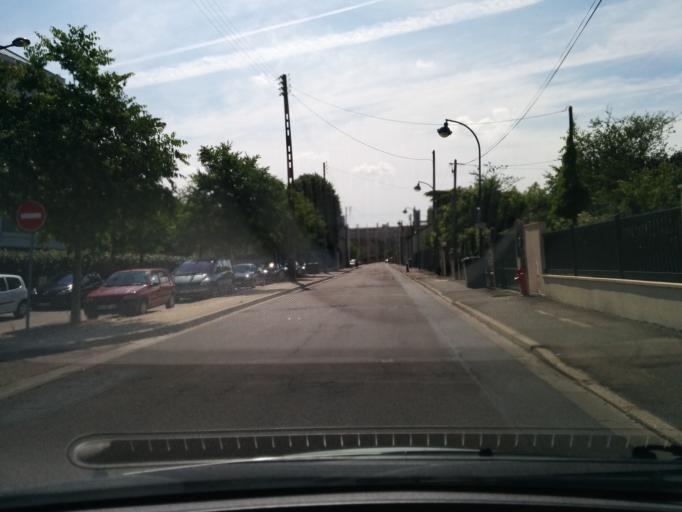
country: FR
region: Ile-de-France
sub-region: Departement des Yvelines
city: Mantes-la-Jolie
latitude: 48.9955
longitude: 1.7129
